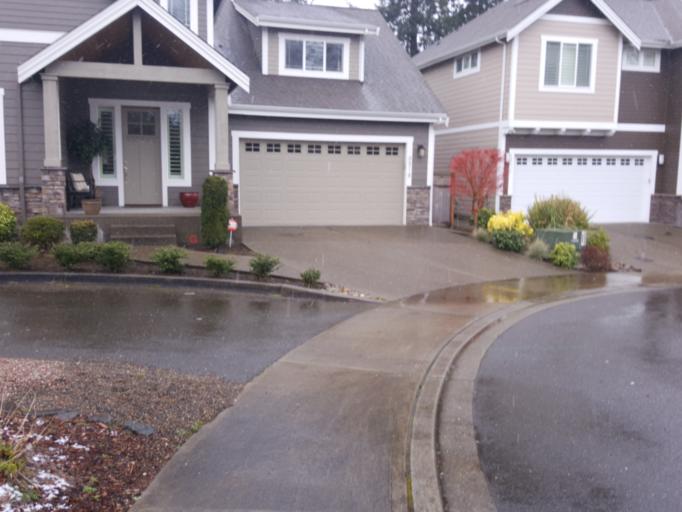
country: US
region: Washington
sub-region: Pierce County
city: University Place
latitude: 47.1975
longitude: -122.5482
